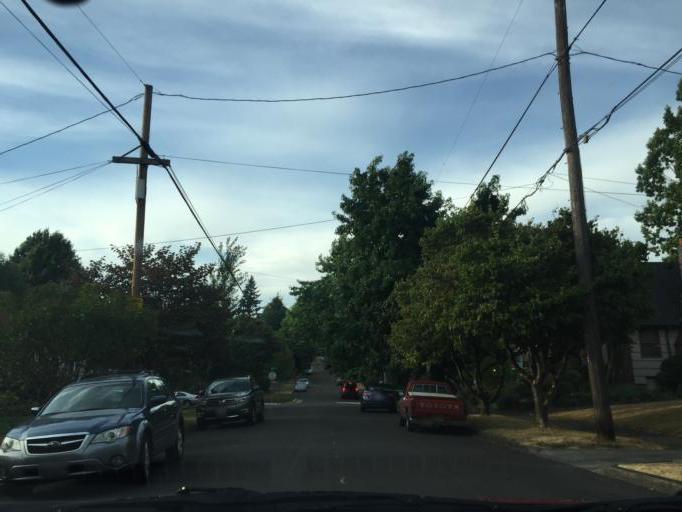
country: US
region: Oregon
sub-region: Multnomah County
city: Portland
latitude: 45.5463
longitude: -122.6327
